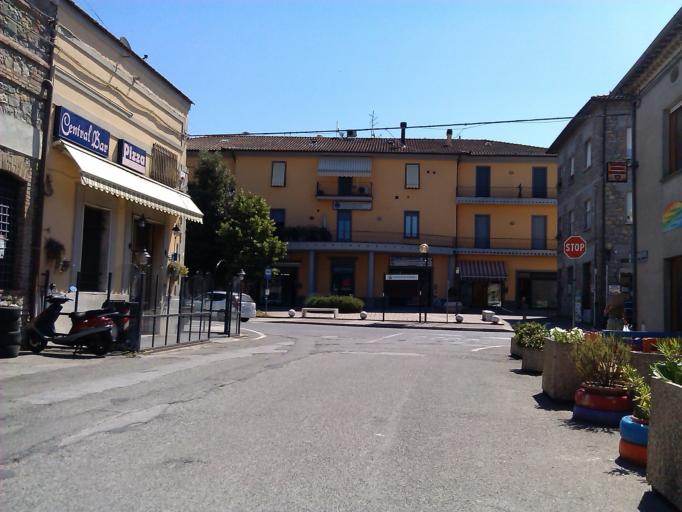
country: IT
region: Umbria
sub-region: Provincia di Terni
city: Fabro Scalo
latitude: 42.8747
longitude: 12.0420
